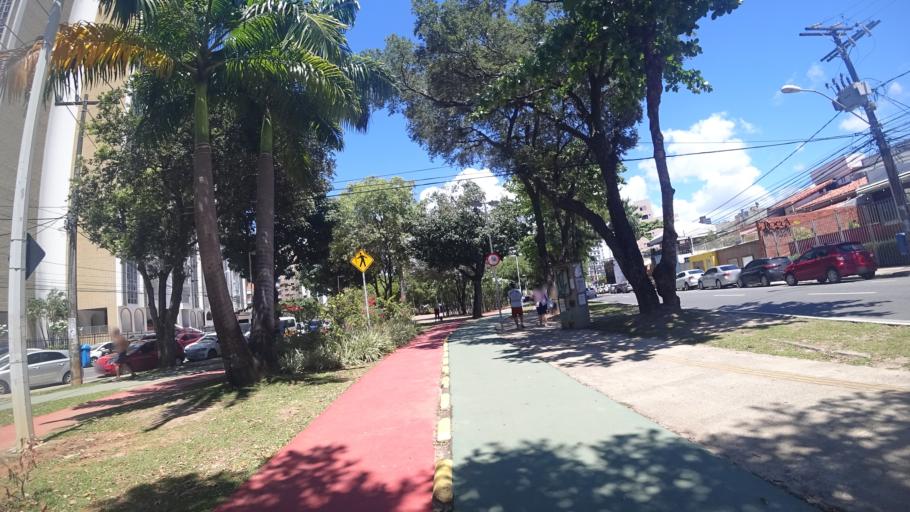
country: BR
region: Bahia
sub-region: Salvador
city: Salvador
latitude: -12.9940
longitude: -38.4603
